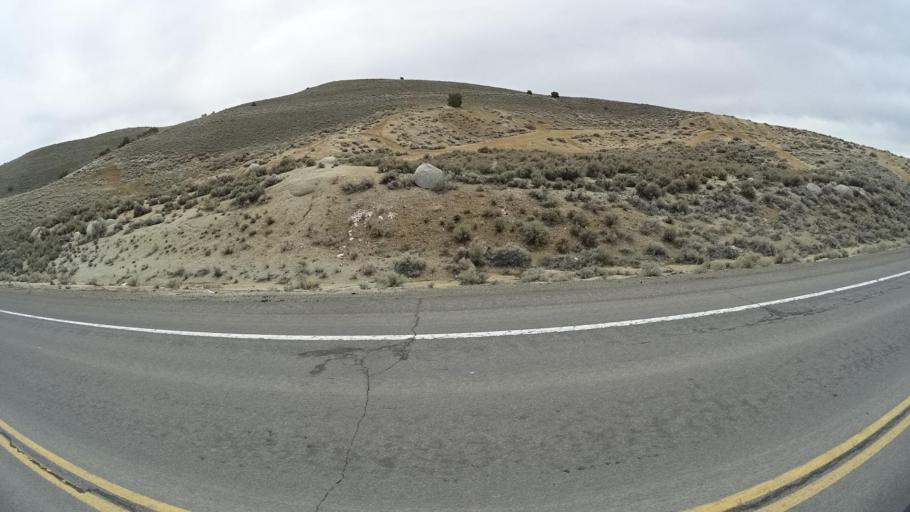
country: US
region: Nevada
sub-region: Washoe County
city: Sun Valley
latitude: 39.6083
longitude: -119.7467
